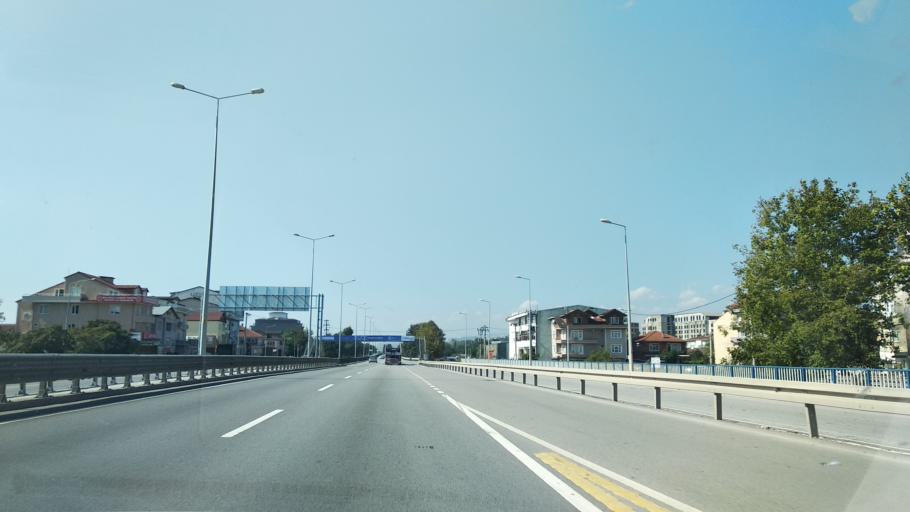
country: TR
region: Kocaeli
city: Kosekoy
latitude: 40.7540
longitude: 30.0197
